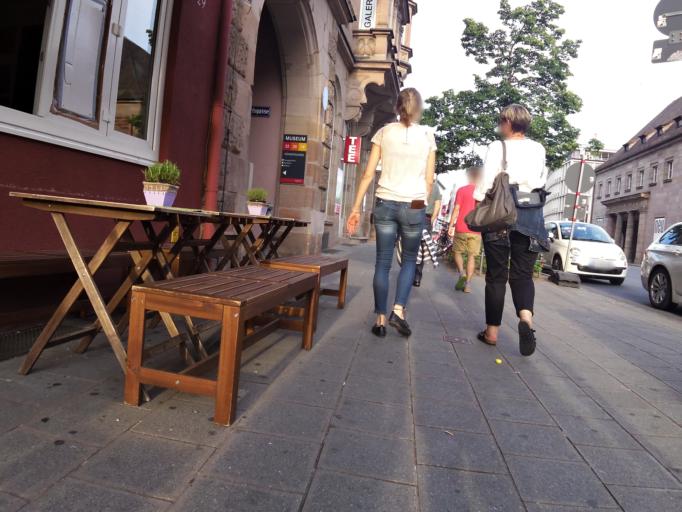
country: DE
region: Bavaria
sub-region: Regierungsbezirk Mittelfranken
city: Nuernberg
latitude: 49.4499
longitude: 11.0821
